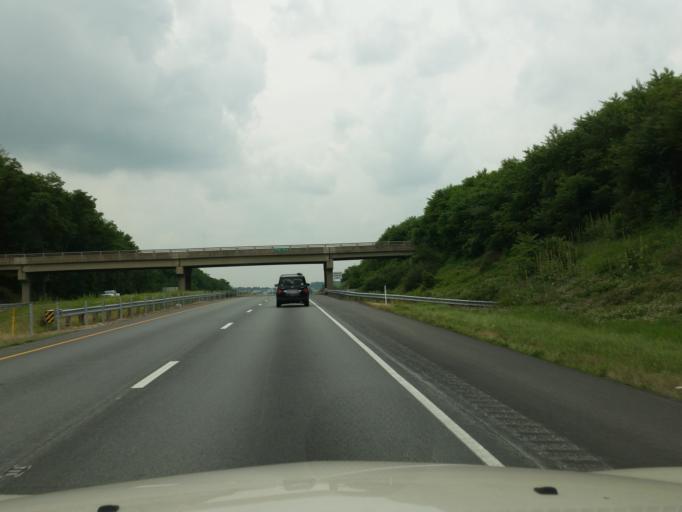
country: US
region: Pennsylvania
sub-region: Lancaster County
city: Rheems
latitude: 40.1548
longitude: -76.5704
